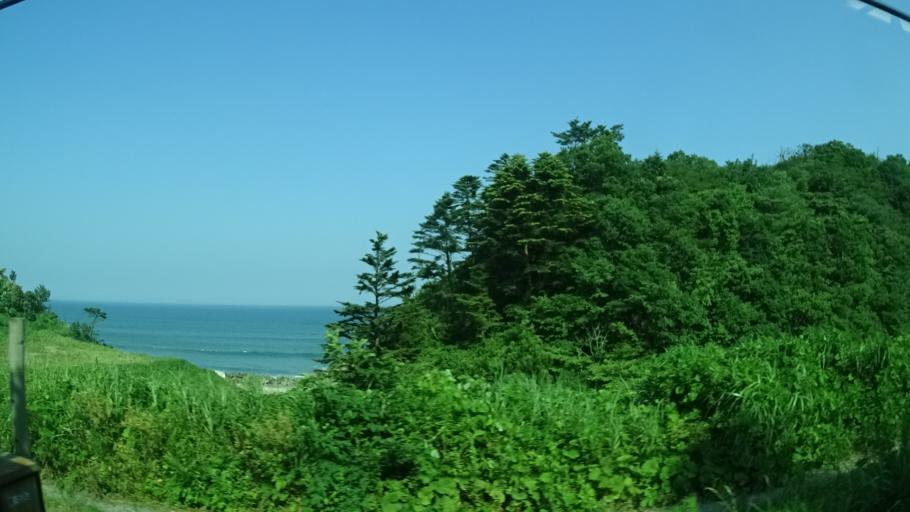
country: JP
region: Fukushima
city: Iwaki
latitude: 37.1836
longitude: 140.9990
